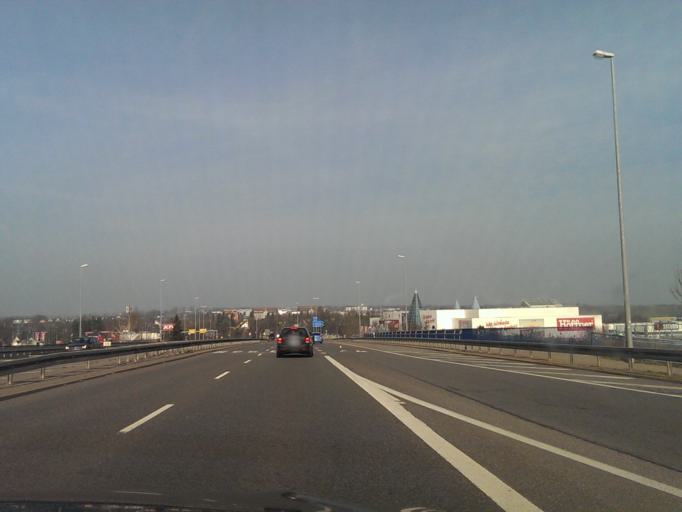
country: DE
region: Saxony
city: Wittgensdorf
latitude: 50.8593
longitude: 12.8682
